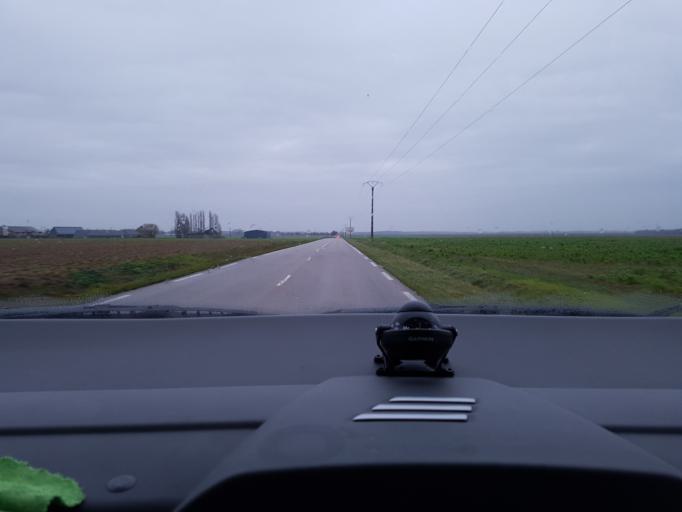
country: FR
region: Haute-Normandie
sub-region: Departement de l'Eure
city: Le Neubourg
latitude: 49.1552
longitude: 0.9887
